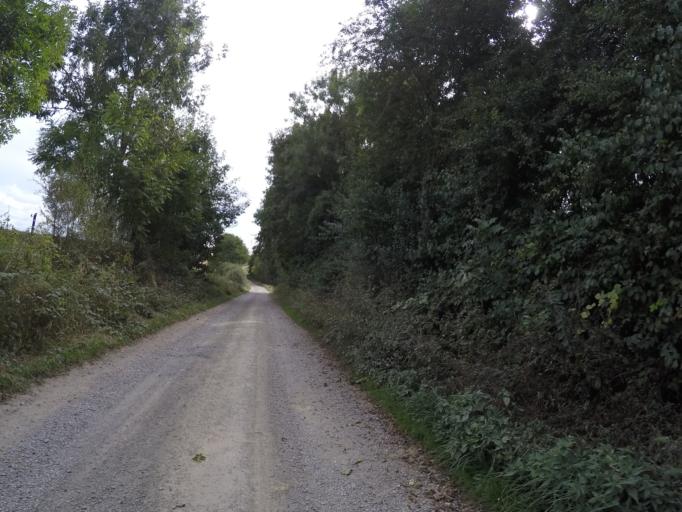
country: BE
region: Wallonia
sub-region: Province de Namur
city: Assesse
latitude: 50.3111
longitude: 4.9774
